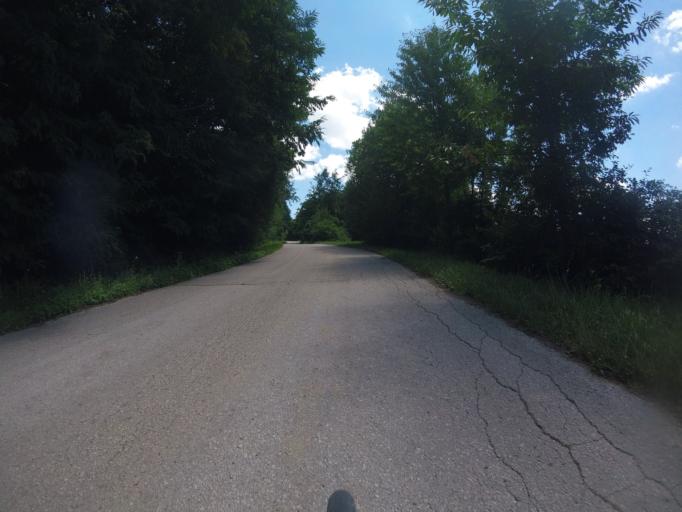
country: HR
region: Karlovacka
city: Ozalj
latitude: 45.6697
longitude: 15.4211
